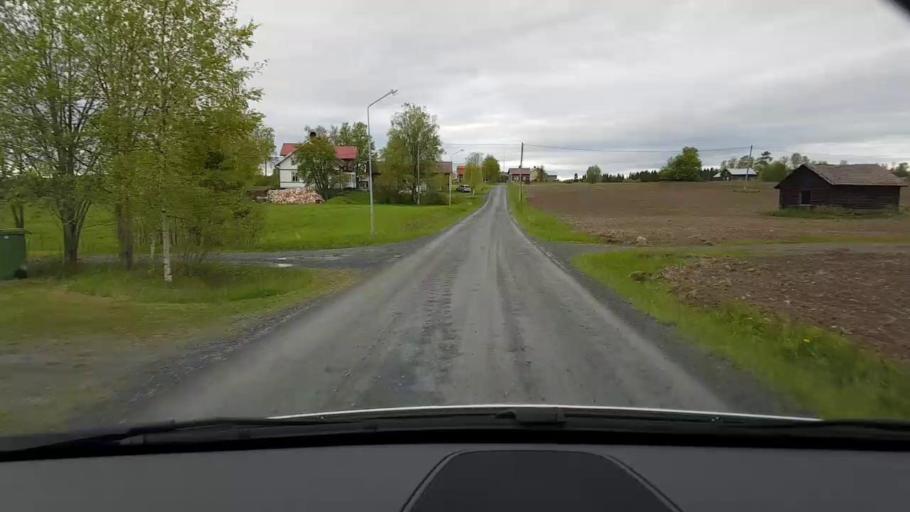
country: SE
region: Jaemtland
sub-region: Krokoms Kommun
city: Valla
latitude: 63.3043
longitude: 14.0162
